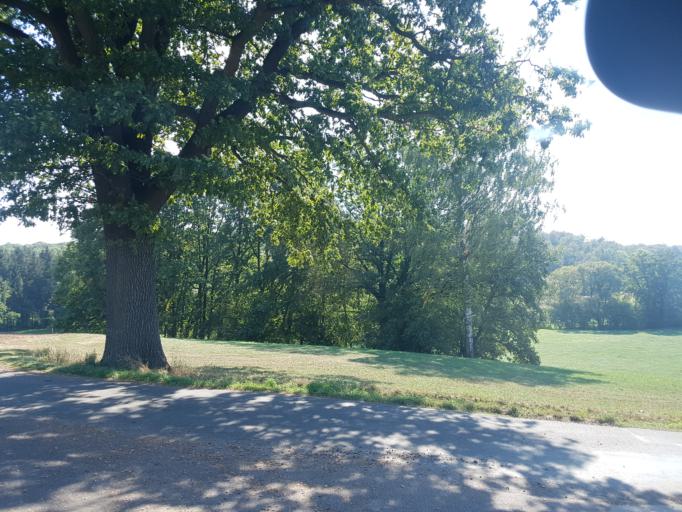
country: DE
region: Saxony
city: Kriebstein
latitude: 51.0493
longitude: 12.9857
